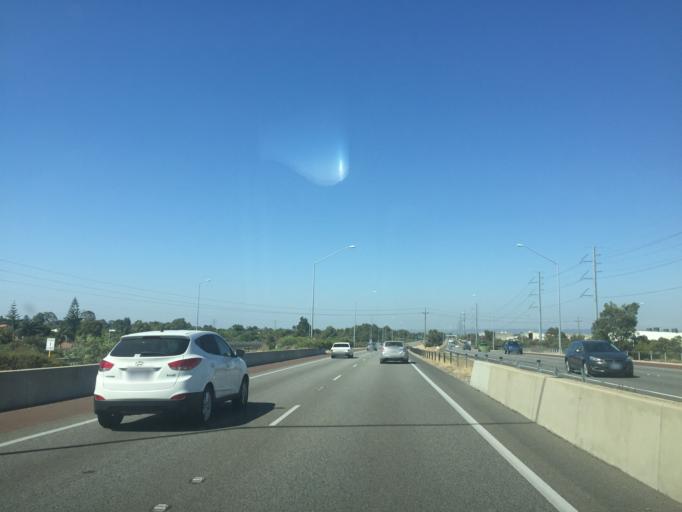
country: AU
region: Western Australia
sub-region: Canning
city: Willetton
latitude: -32.0681
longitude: 115.8909
